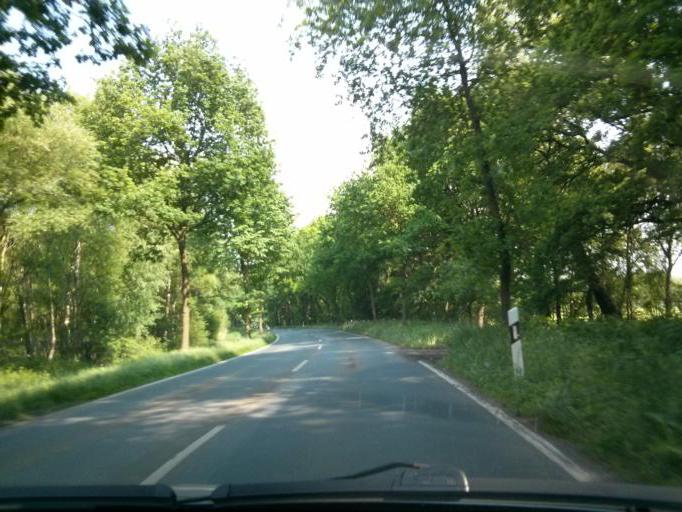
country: DE
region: Lower Saxony
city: Schiffdorf
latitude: 53.5167
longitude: 8.6791
